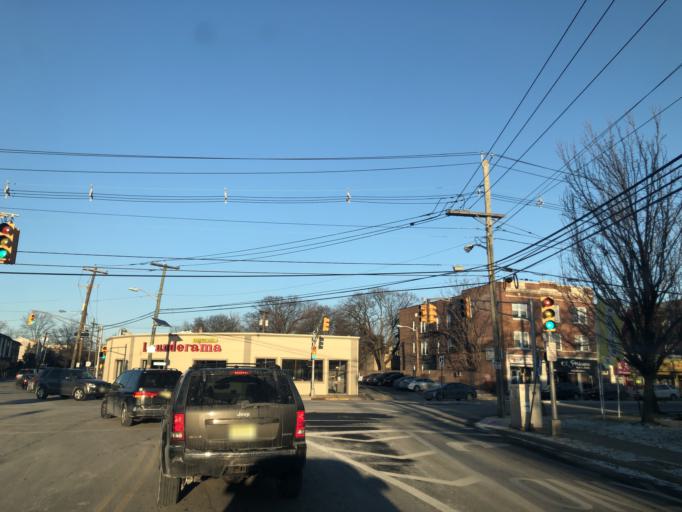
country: US
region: New Jersey
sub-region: Union County
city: Union
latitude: 40.7148
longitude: -74.2527
